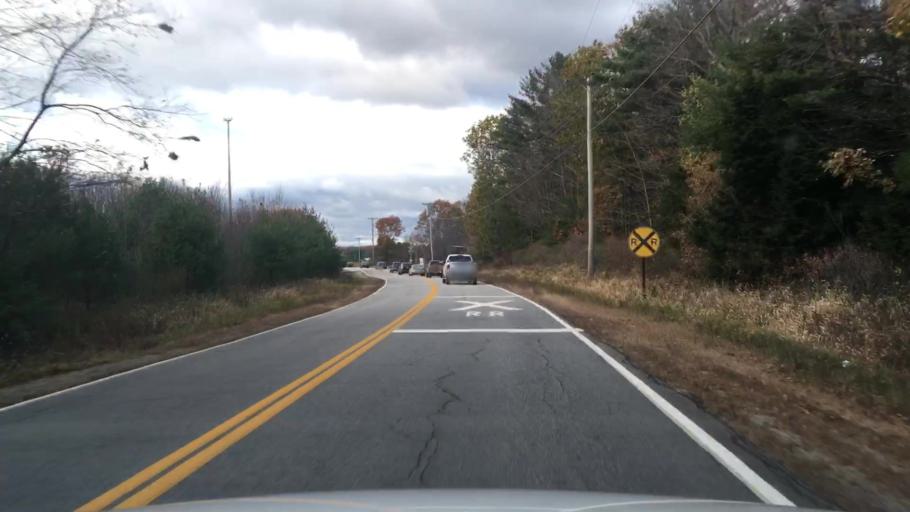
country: US
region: Maine
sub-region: Androscoggin County
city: Leeds
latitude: 44.3304
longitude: -70.1239
